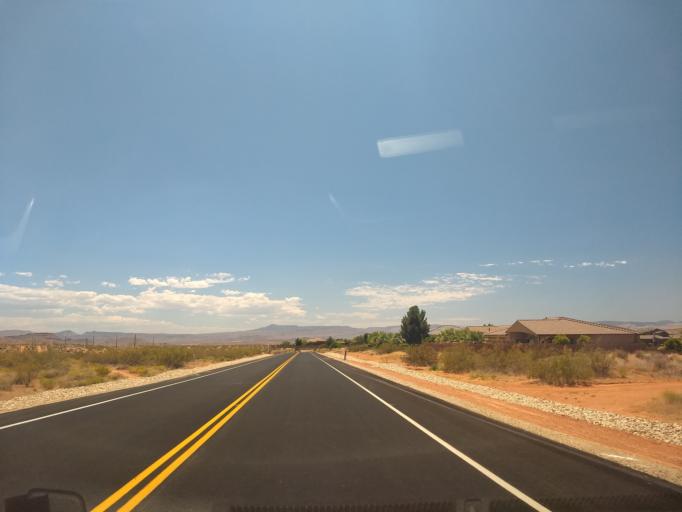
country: US
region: Utah
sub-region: Washington County
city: Washington
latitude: 37.1572
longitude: -113.5195
